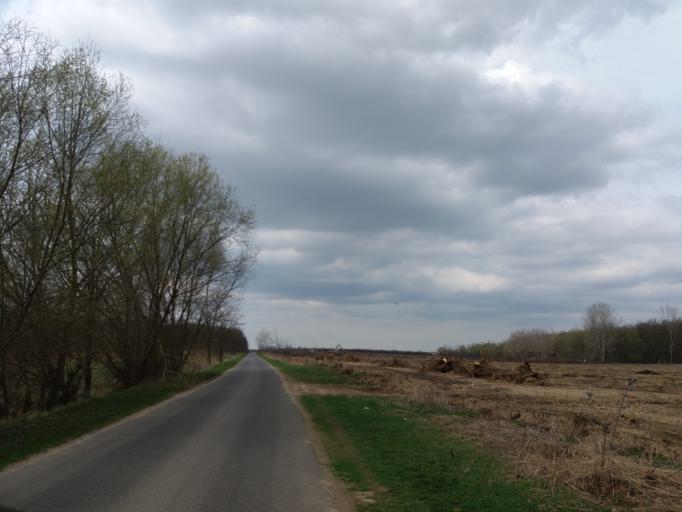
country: HU
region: Szabolcs-Szatmar-Bereg
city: Nyirtass
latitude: 48.0867
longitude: 22.0366
